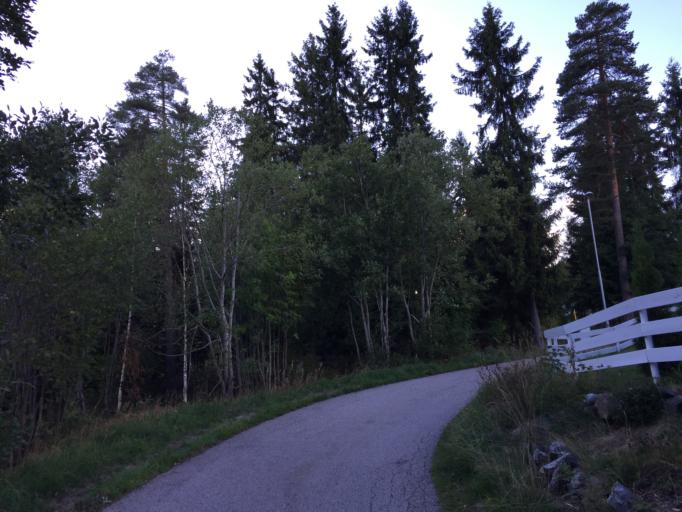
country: NO
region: Akershus
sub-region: Raelingen
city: Fjerdingby
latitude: 59.9307
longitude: 11.0433
